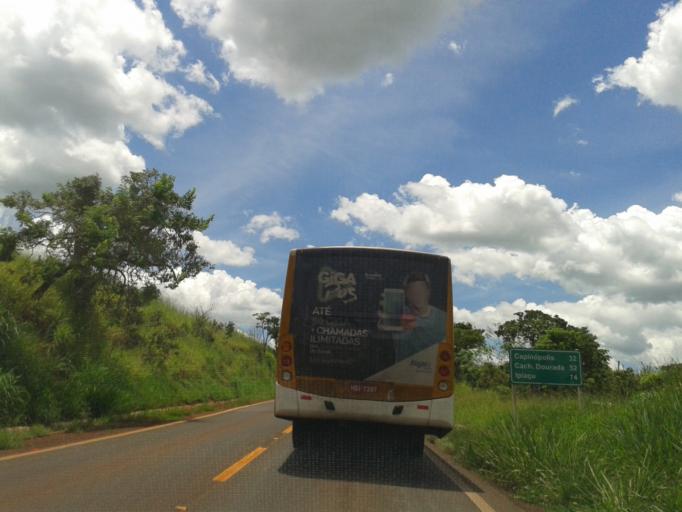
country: BR
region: Minas Gerais
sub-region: Ituiutaba
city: Ituiutaba
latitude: -18.9351
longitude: -49.4452
